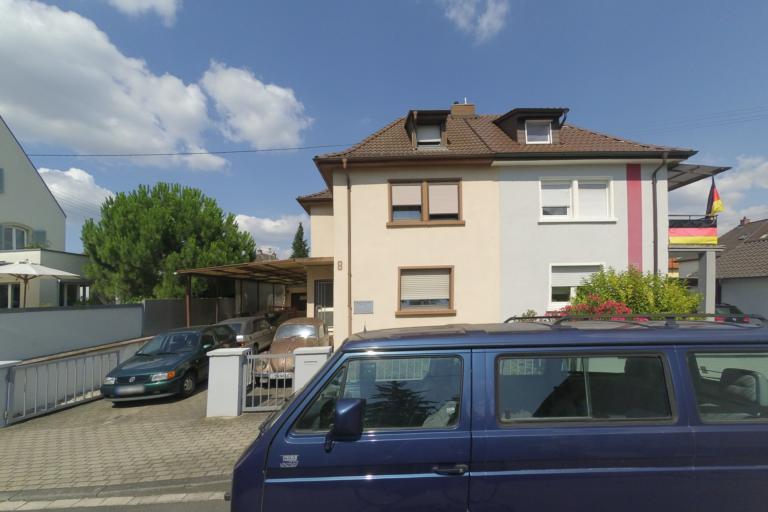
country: DE
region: Rheinland-Pfalz
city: Frankenthal
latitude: 49.5161
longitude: 8.3985
